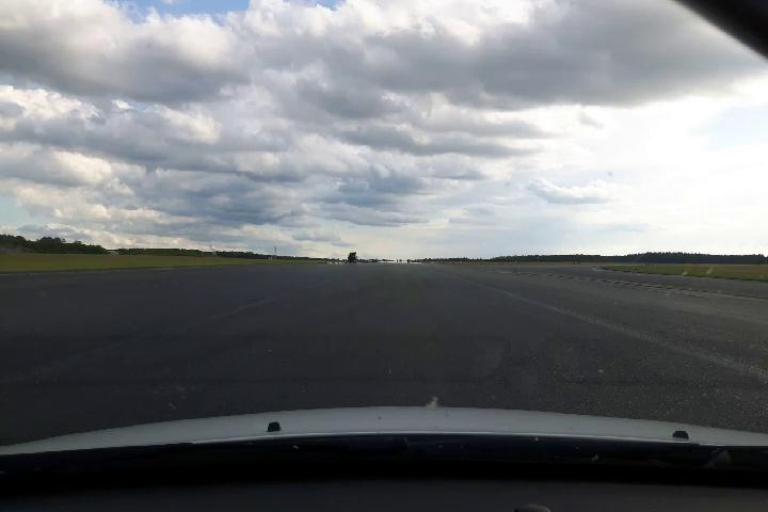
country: SE
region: Stockholm
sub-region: Sigtuna Kommun
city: Rosersberg
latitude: 59.6345
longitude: 17.9534
